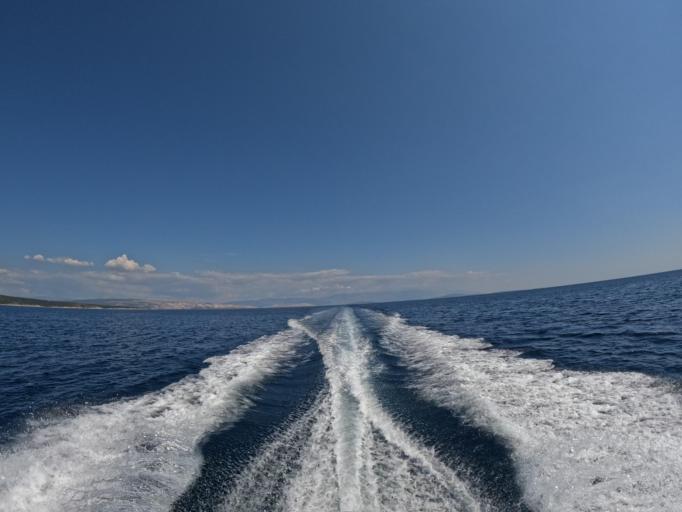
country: HR
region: Primorsko-Goranska
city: Cres
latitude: 44.9412
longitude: 14.4873
